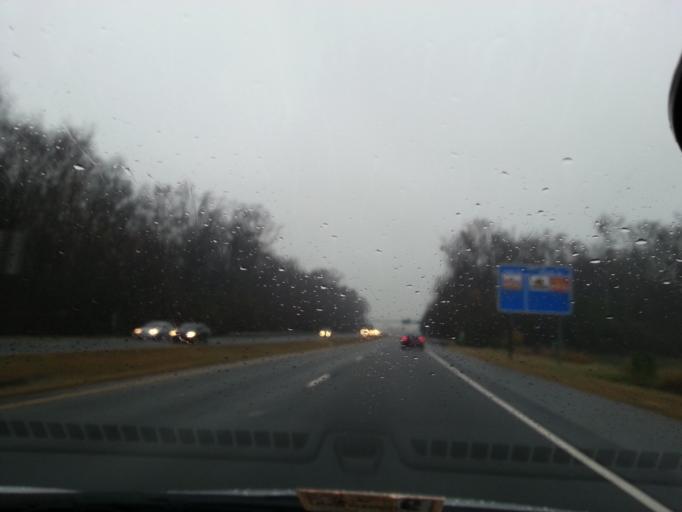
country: US
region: North Carolina
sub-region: Currituck County
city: Moyock
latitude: 36.6660
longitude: -76.2305
